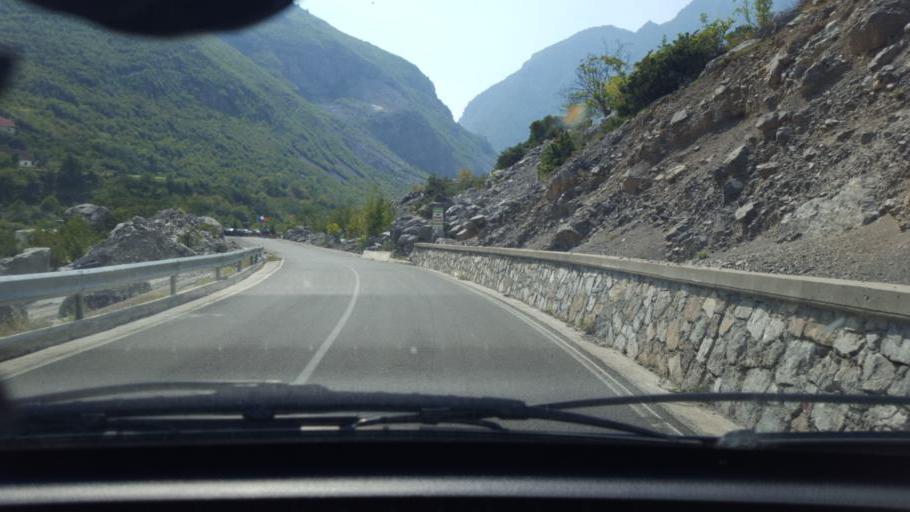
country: AL
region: Shkoder
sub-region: Rrethi i Malesia e Madhe
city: Kastrat
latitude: 42.5060
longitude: 19.5982
